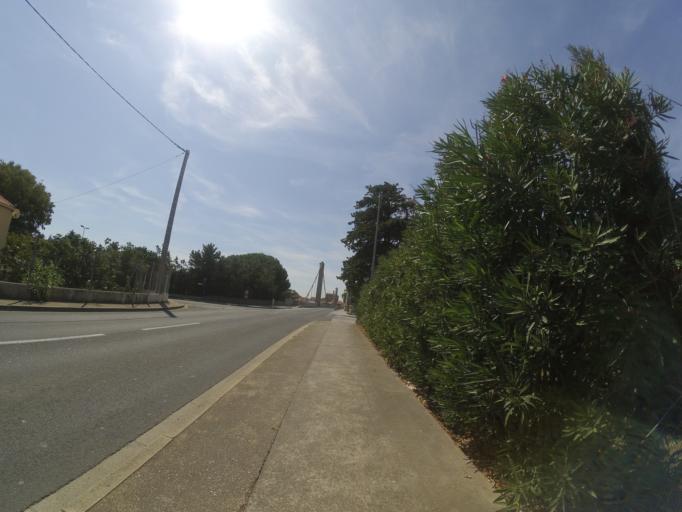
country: FR
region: Languedoc-Roussillon
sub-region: Departement des Pyrenees-Orientales
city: Rivesaltes
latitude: 42.7730
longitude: 2.8716
